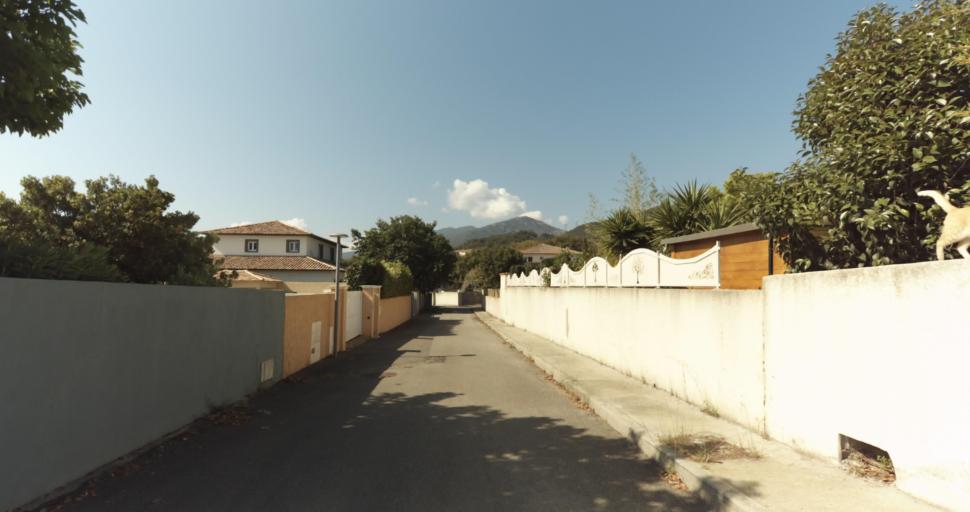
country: FR
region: Corsica
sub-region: Departement de la Haute-Corse
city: Biguglia
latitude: 42.6254
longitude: 9.4271
